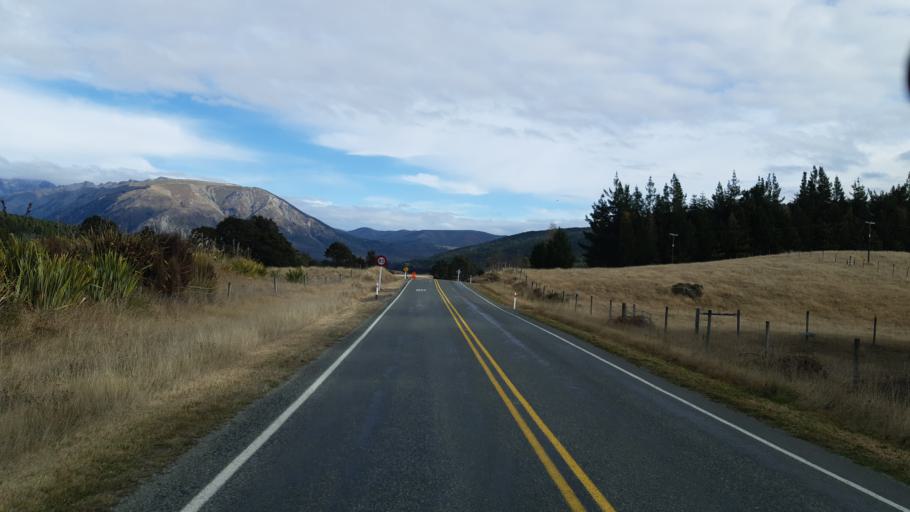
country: NZ
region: Tasman
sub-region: Tasman District
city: Wakefield
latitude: -41.7871
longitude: 172.8886
